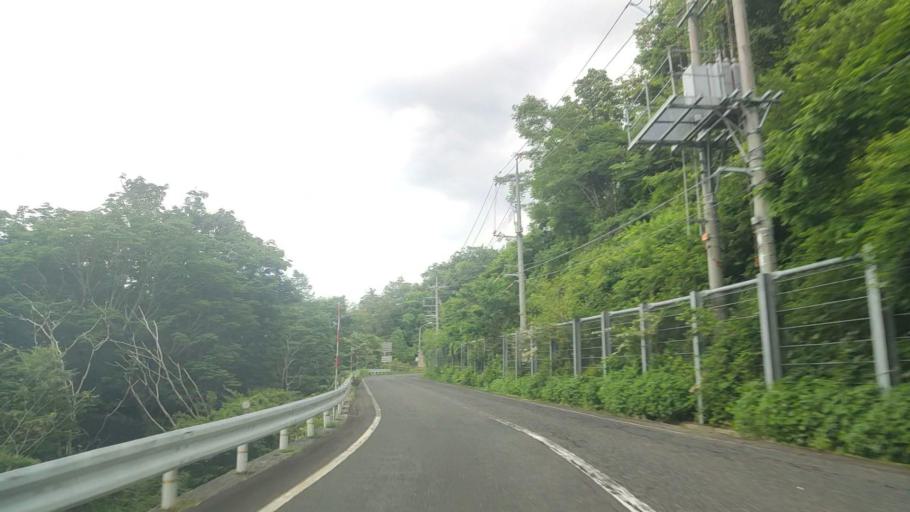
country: JP
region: Tottori
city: Kurayoshi
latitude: 35.3136
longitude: 134.0027
